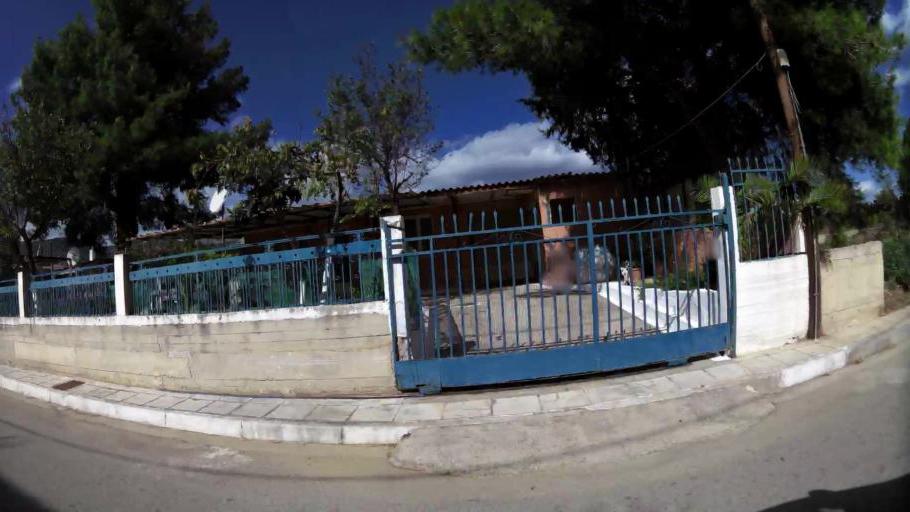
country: GR
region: Attica
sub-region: Nomarchia Anatolikis Attikis
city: Thrakomakedones
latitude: 38.1106
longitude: 23.7412
